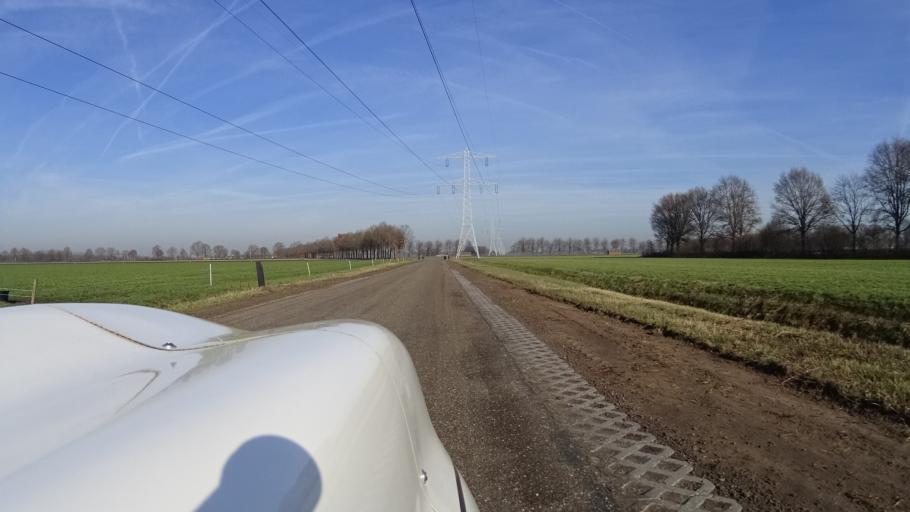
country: NL
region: North Brabant
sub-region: Gemeente Boekel
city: Boekel
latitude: 51.6068
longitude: 5.6494
